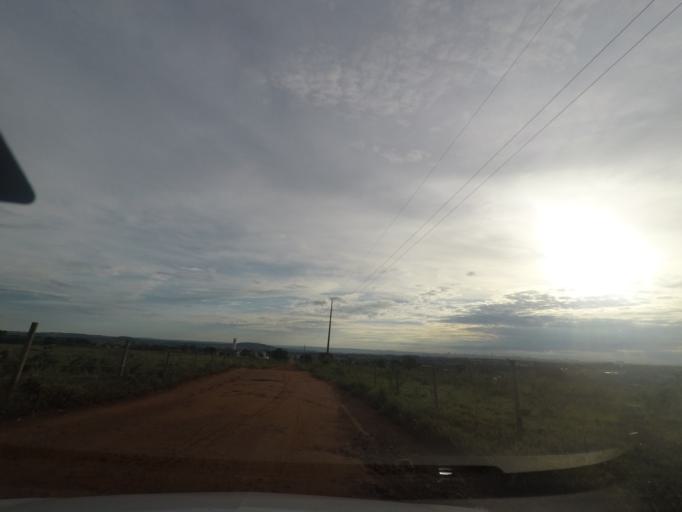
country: BR
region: Goias
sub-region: Trindade
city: Trindade
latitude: -16.7321
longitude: -49.4137
